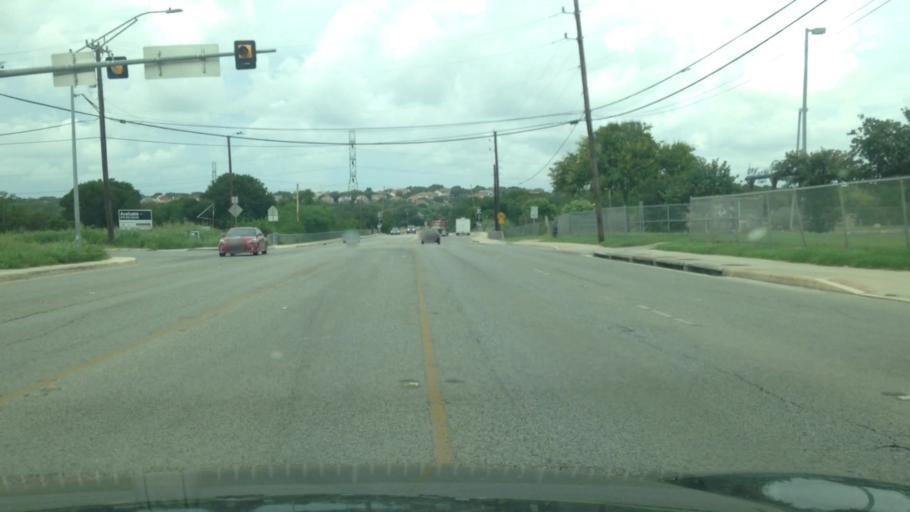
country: US
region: Texas
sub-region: Bexar County
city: Live Oak
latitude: 29.5831
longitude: -98.3942
